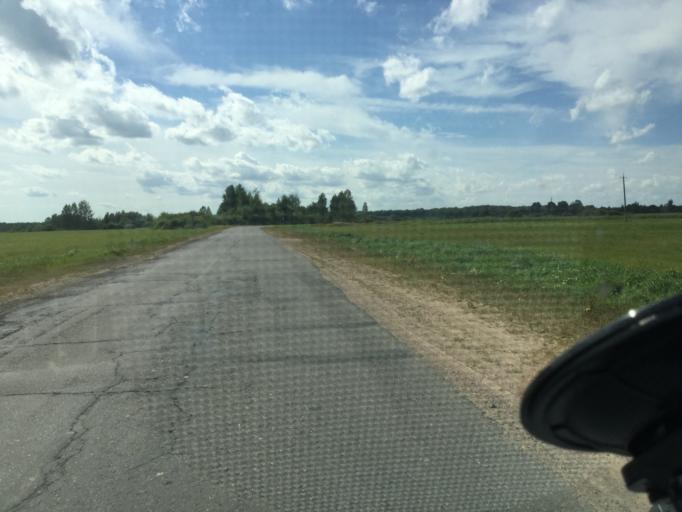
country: BY
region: Vitebsk
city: Chashniki
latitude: 55.3125
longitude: 29.4181
